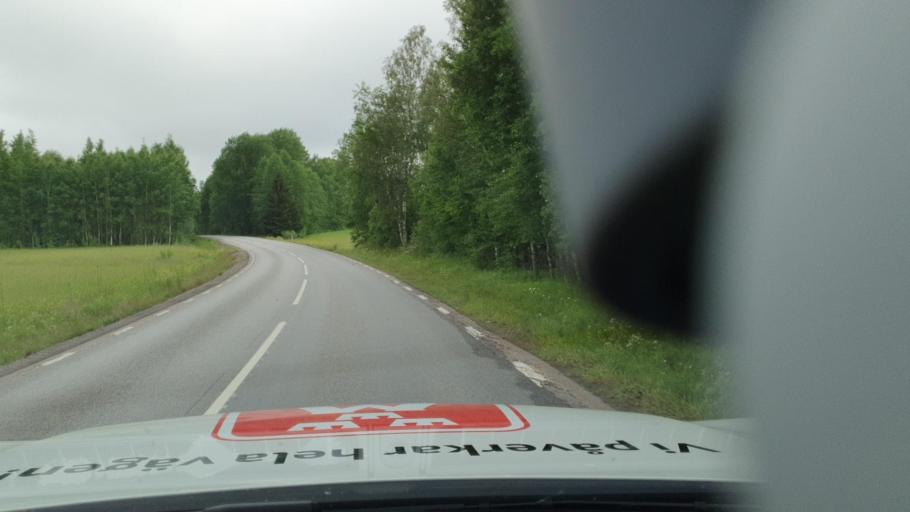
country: SE
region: Vaermland
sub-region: Kristinehamns Kommun
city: Bjorneborg
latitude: 59.1014
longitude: 14.2560
